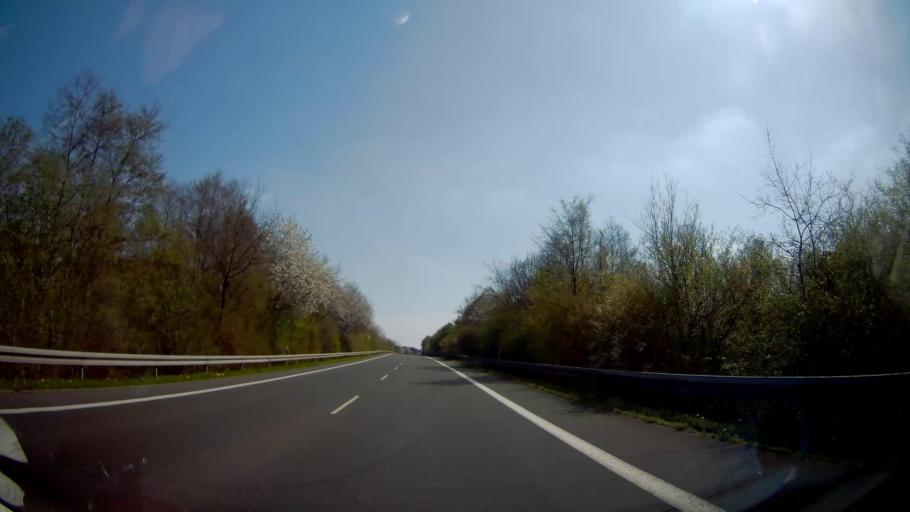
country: DE
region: North Rhine-Westphalia
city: Dorsten
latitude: 51.6879
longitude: 7.0148
